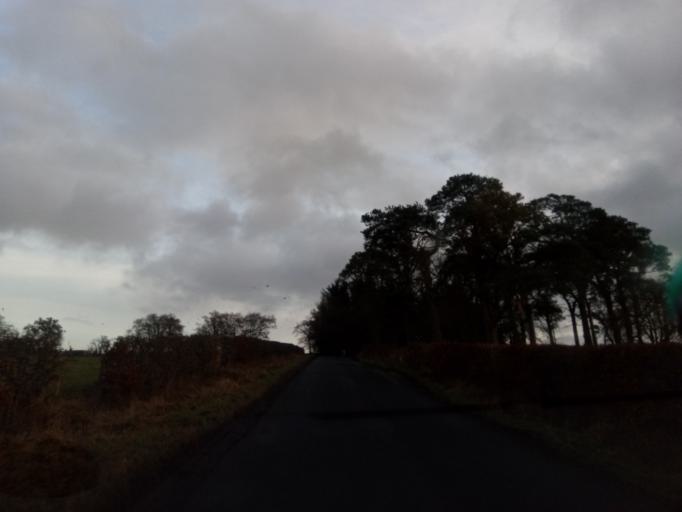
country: GB
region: Scotland
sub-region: The Scottish Borders
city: Melrose
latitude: 55.5506
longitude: -2.7713
